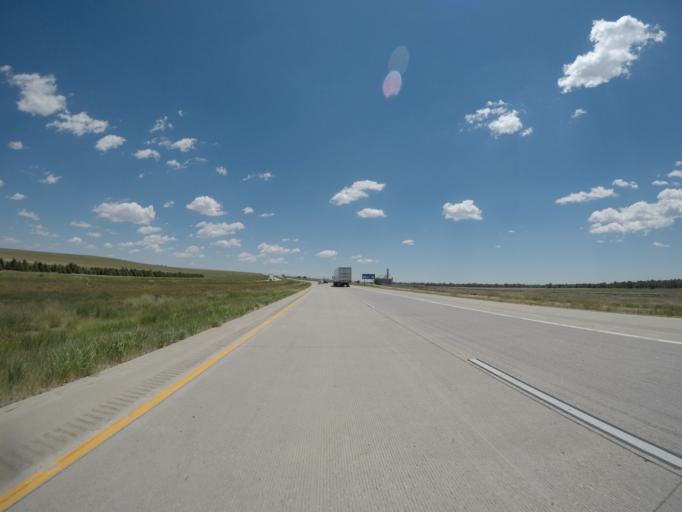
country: US
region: Colorado
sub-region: Lincoln County
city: Limon
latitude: 39.2734
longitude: -103.7363
